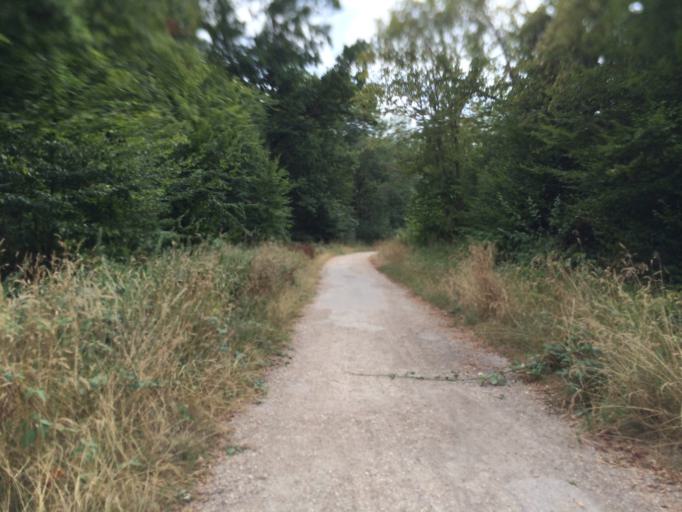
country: FR
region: Ile-de-France
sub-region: Departement de l'Essonne
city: Quincy-sous-Senart
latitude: 48.6598
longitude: 2.5438
